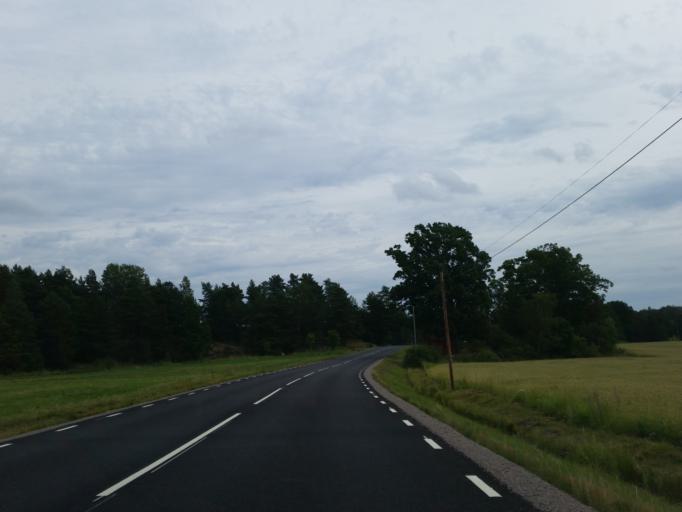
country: SE
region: Soedermanland
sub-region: Strangnas Kommun
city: Akers Styckebruk
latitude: 59.2732
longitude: 17.1410
